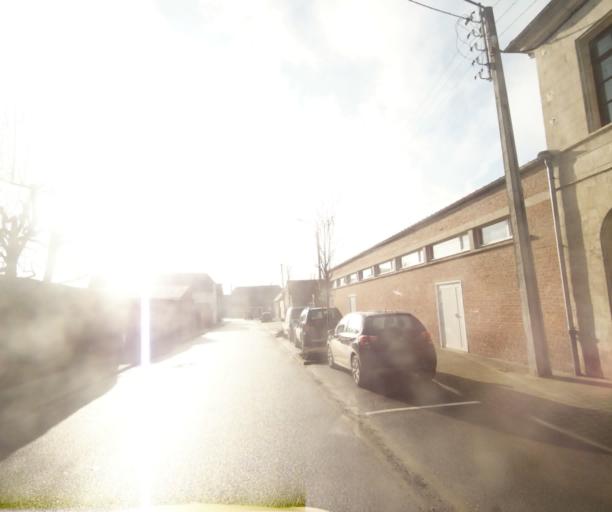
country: FR
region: Nord-Pas-de-Calais
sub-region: Departement du Nord
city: Thiant
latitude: 50.2865
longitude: 3.4551
